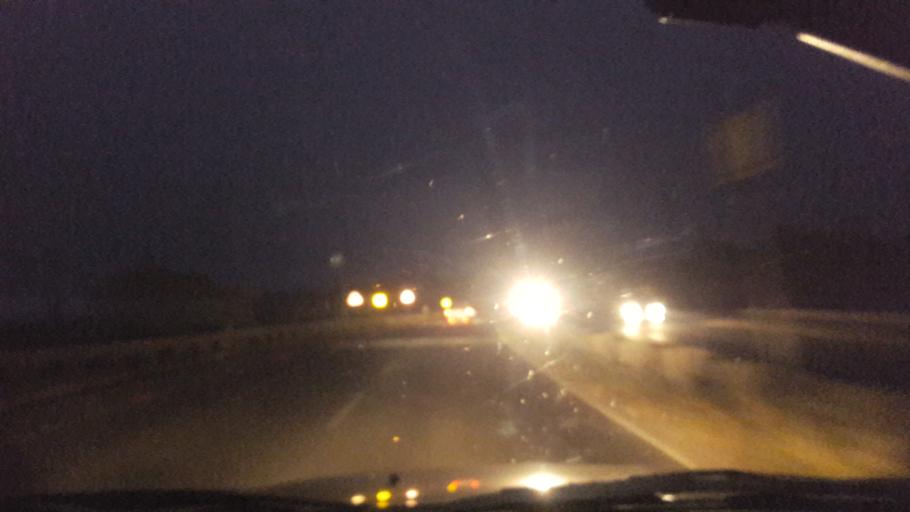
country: IN
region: Andhra Pradesh
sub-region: East Godavari
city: Peddapuram
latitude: 17.1377
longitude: 81.9613
